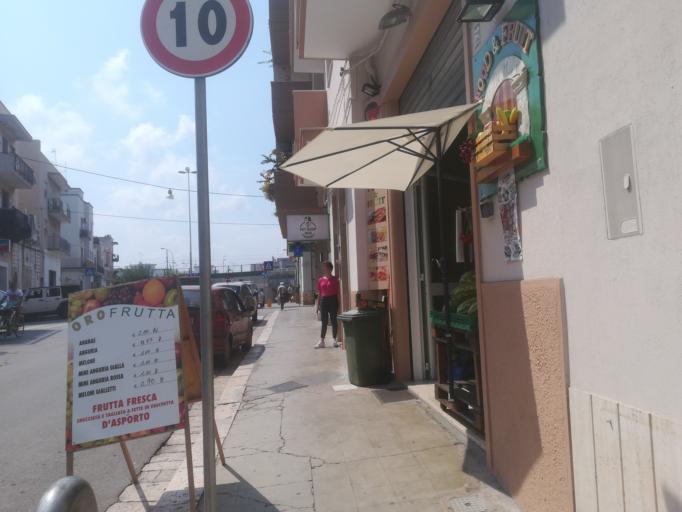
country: IT
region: Apulia
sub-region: Provincia di Bari
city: Polignano a Mare
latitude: 40.9929
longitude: 17.2177
